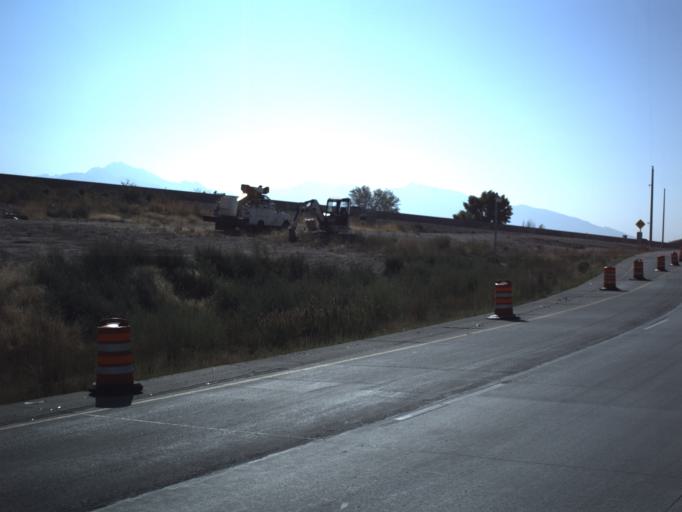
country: US
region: Utah
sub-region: Salt Lake County
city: Taylorsville
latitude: 40.6959
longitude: -111.9535
